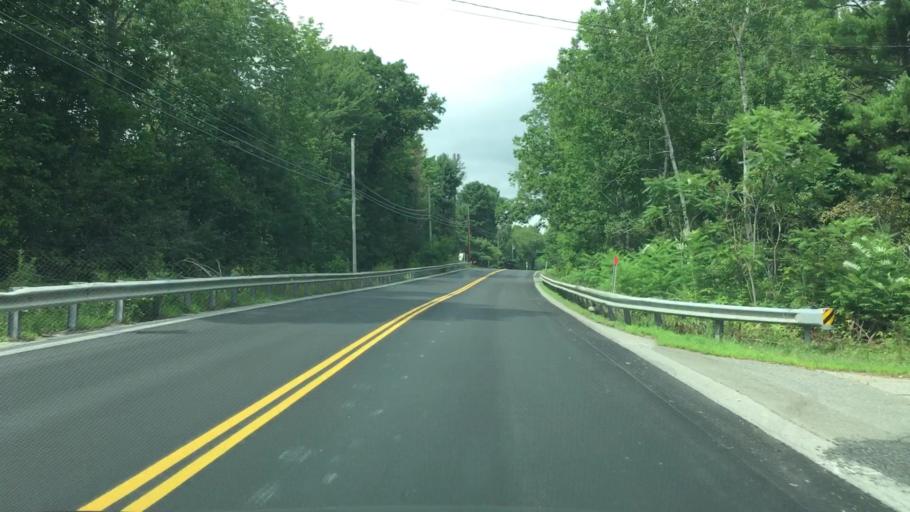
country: US
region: Maine
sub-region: Hancock County
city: Bucksport
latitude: 44.5987
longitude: -68.8146
